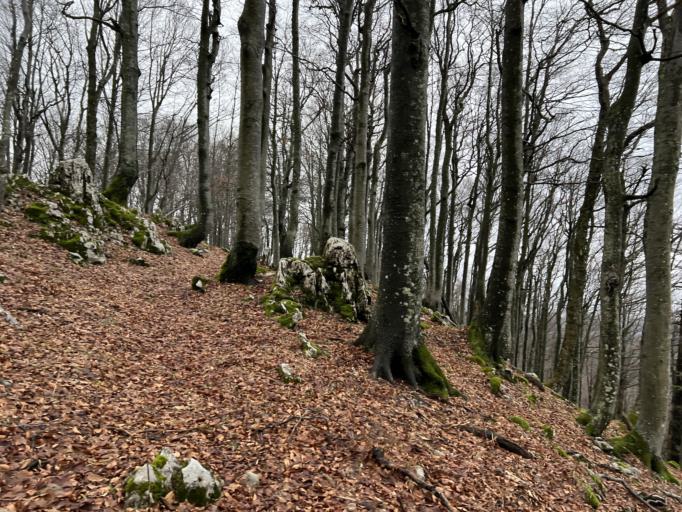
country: SI
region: Ajdovscina
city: Lokavec
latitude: 45.9521
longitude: 13.8329
